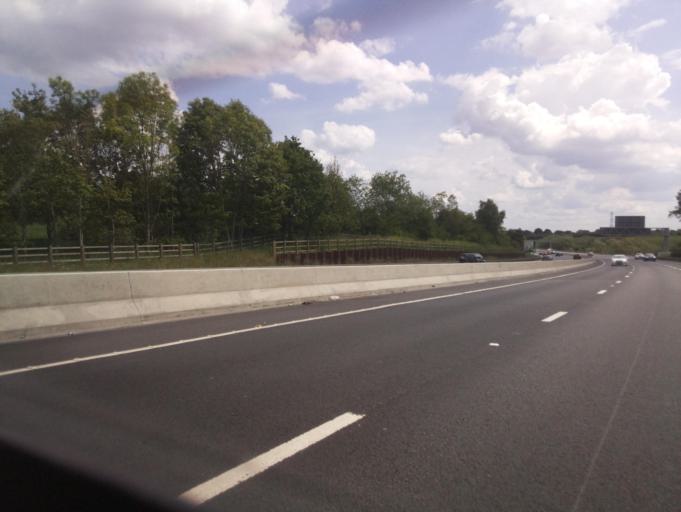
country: GB
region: England
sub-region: Stockton-on-Tees
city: Billingham
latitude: 54.6076
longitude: -1.3184
